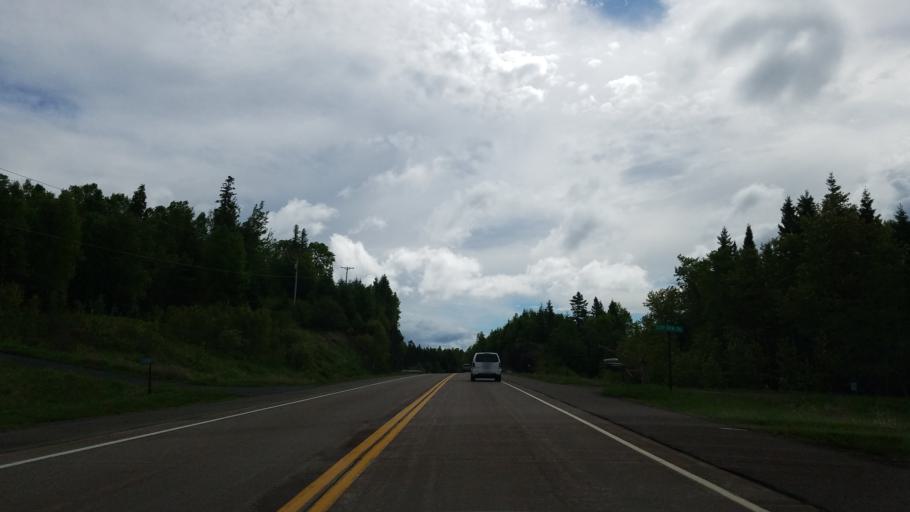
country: US
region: Minnesota
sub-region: Lake County
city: Two Harbors
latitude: 47.1023
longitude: -91.5427
